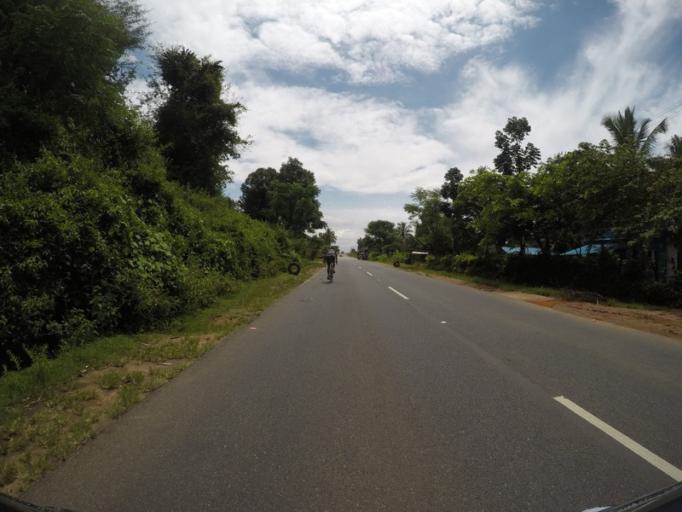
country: IN
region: Karnataka
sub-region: Kodagu
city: Kushalnagar
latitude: 12.4413
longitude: 75.9135
